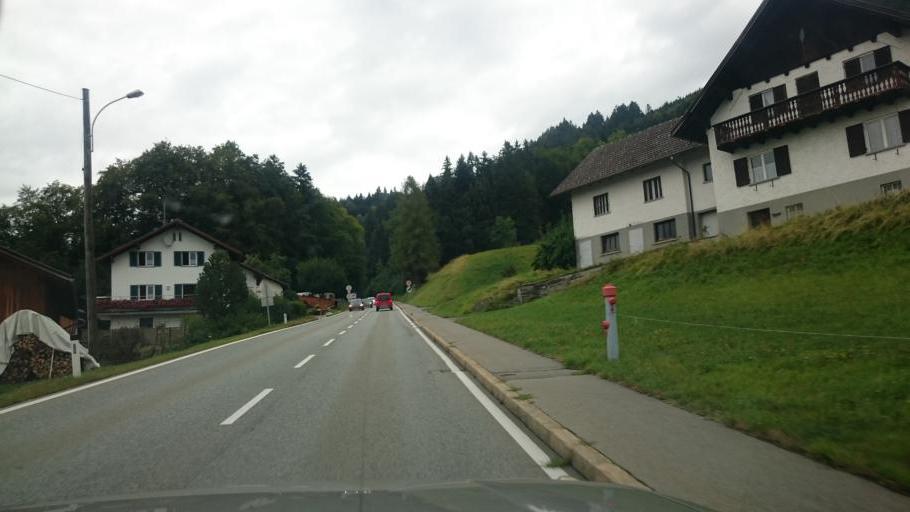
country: AT
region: Vorarlberg
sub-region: Politischer Bezirk Dornbirn
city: Dornbirn
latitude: 47.4170
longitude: 9.7677
